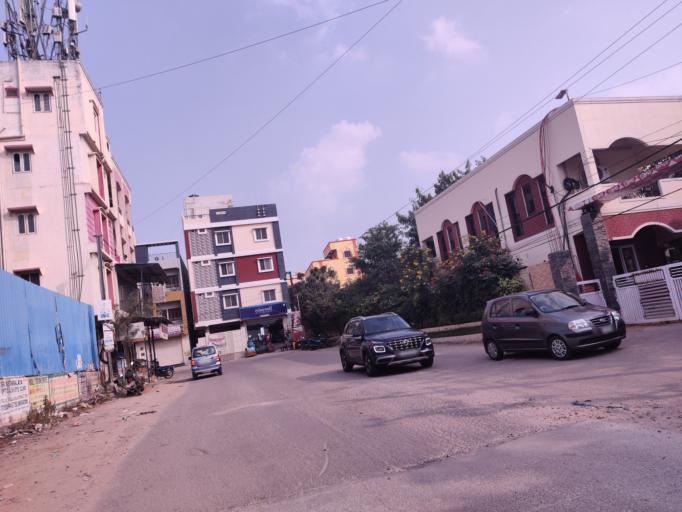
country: IN
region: Telangana
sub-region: Hyderabad
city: Hyderabad
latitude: 17.4032
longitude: 78.3906
